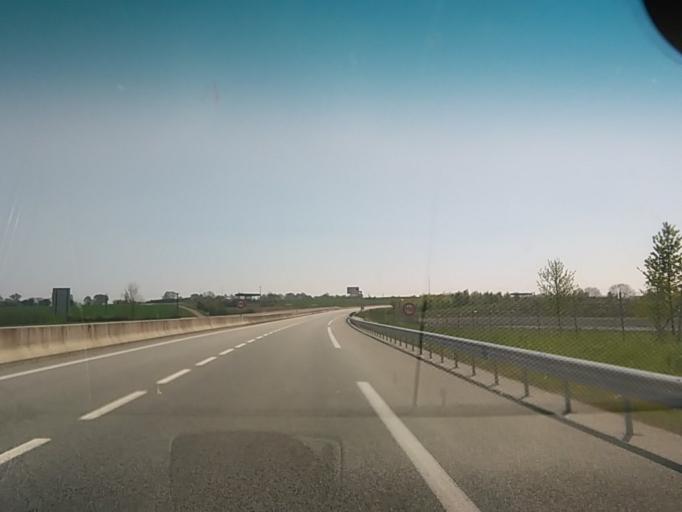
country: FR
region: Lower Normandy
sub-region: Departement de l'Orne
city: Sees
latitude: 48.6404
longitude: 0.1781
